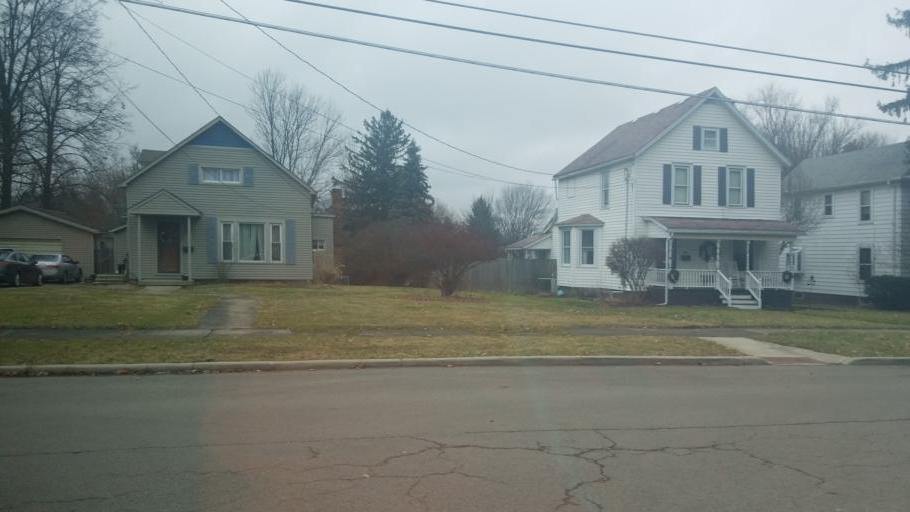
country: US
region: Ohio
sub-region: Crawford County
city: Galion
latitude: 40.7363
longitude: -82.7843
